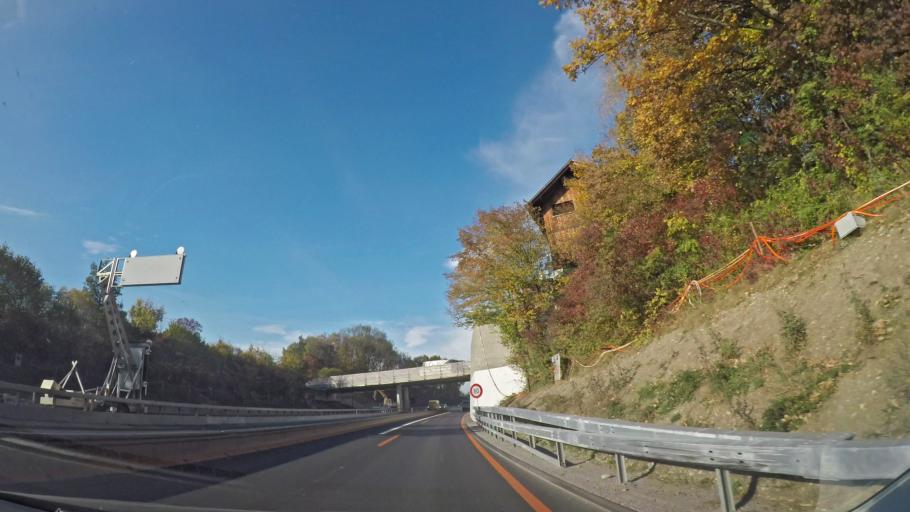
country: CH
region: Bern
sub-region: Thun District
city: Thierachern
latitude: 46.7614
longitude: 7.5944
